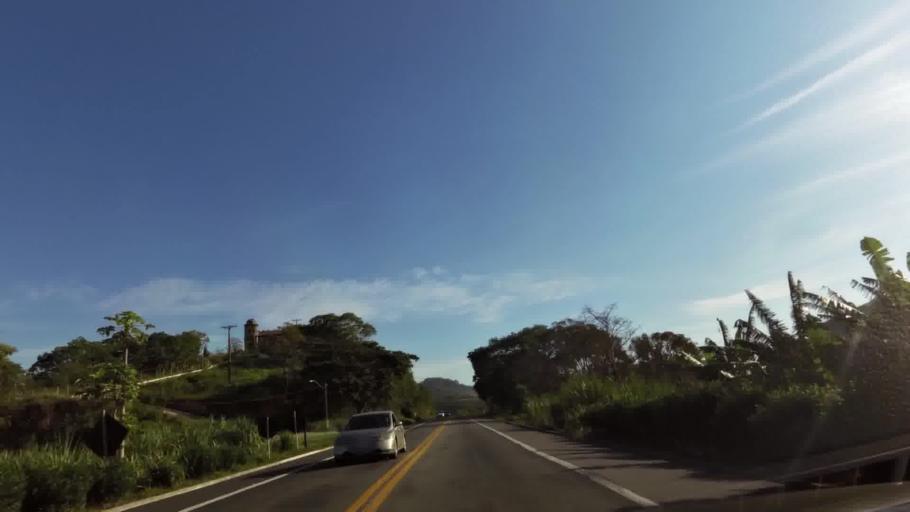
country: BR
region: Espirito Santo
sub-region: Viana
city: Viana
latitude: -20.4190
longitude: -40.4597
